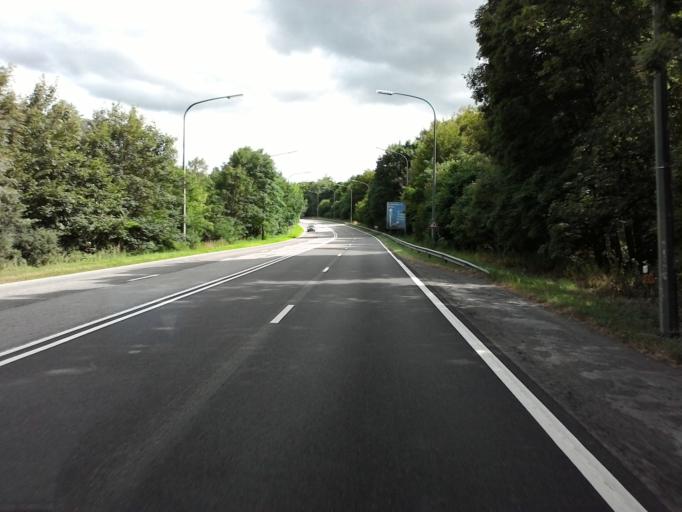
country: BE
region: Wallonia
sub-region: Province du Luxembourg
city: Martelange
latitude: 49.7920
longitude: 5.7422
